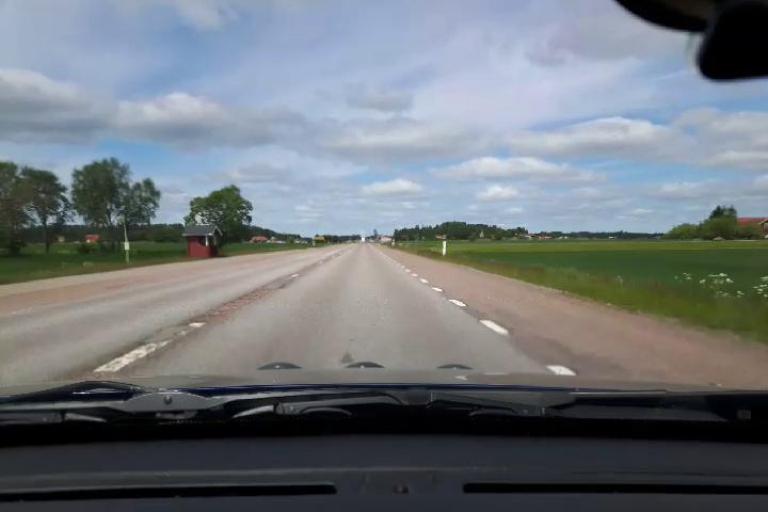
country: SE
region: Uppsala
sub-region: Uppsala Kommun
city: Gamla Uppsala
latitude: 59.9258
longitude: 17.6001
